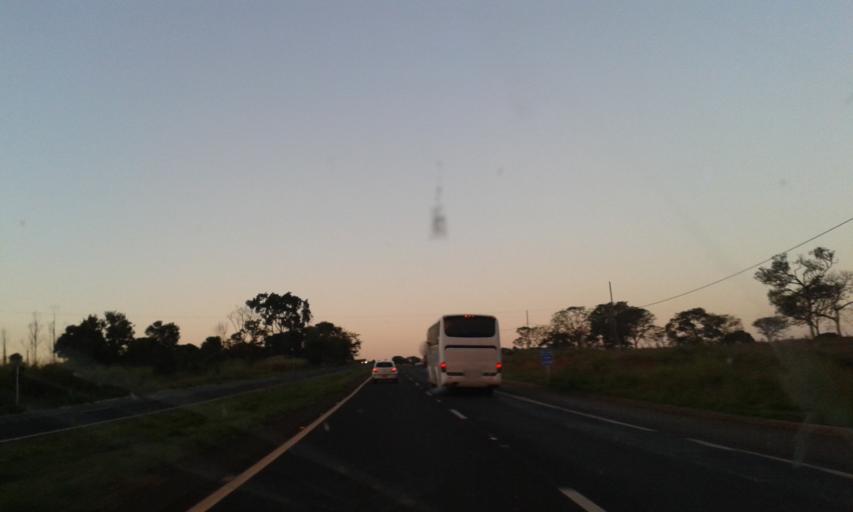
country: BR
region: Minas Gerais
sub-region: Monte Alegre De Minas
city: Monte Alegre de Minas
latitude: -18.8766
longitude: -48.6027
